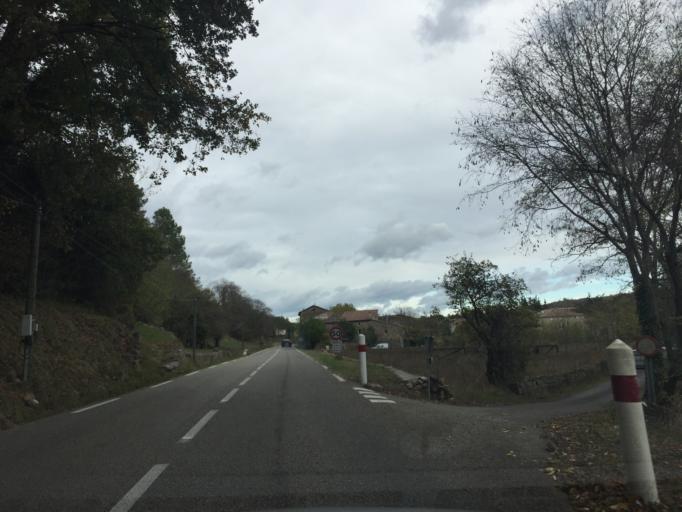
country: FR
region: Rhone-Alpes
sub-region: Departement de l'Ardeche
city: Lablachere
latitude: 44.4289
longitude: 4.1844
